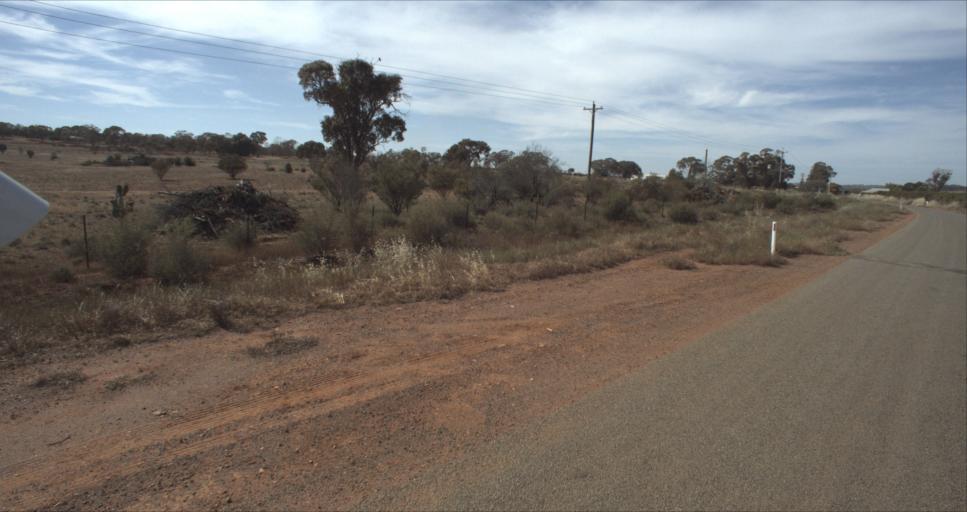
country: AU
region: New South Wales
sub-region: Leeton
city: Leeton
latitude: -34.5843
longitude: 146.4765
